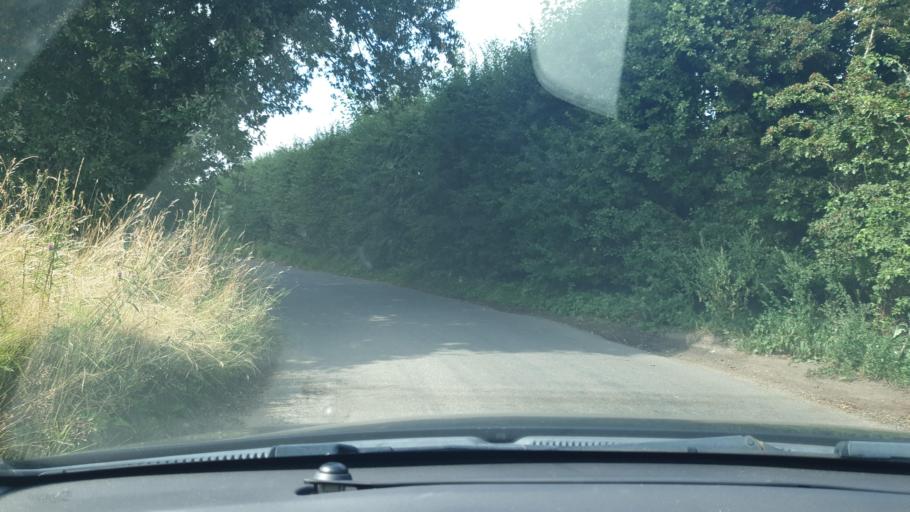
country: GB
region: England
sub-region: Suffolk
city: East Bergholt
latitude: 51.9238
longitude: 0.9995
